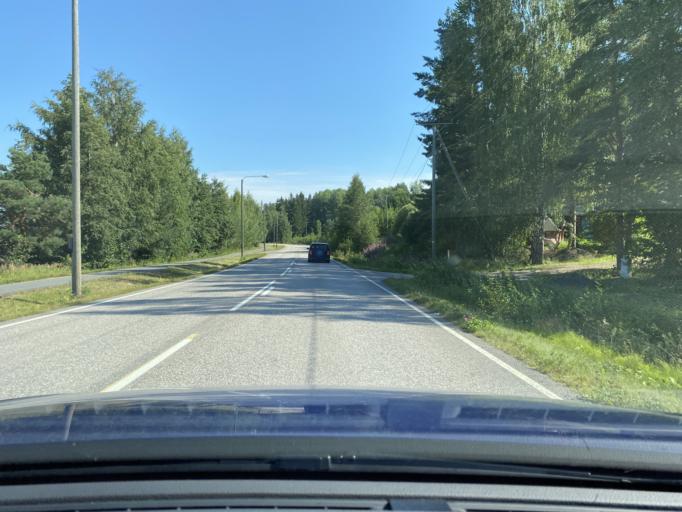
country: FI
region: Central Finland
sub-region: Jaemsae
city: Jaemsae
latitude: 61.8862
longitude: 25.2983
